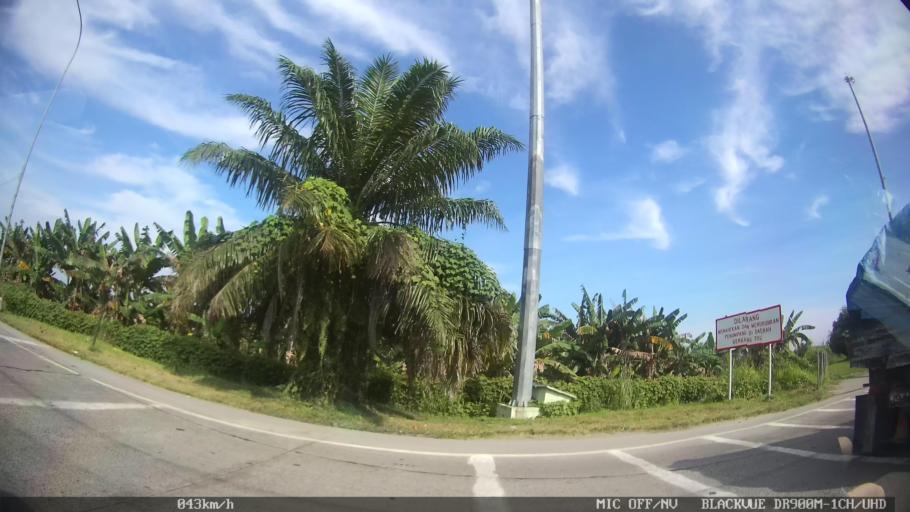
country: ID
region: North Sumatra
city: Sunggal
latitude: 3.6299
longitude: 98.6318
